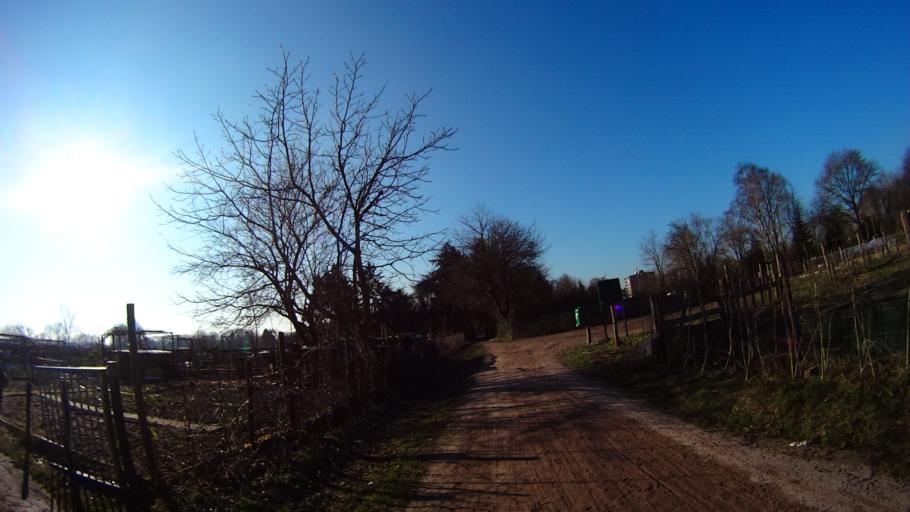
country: NL
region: Utrecht
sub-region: Gemeente Soest
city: Soest
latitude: 52.1723
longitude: 5.2964
